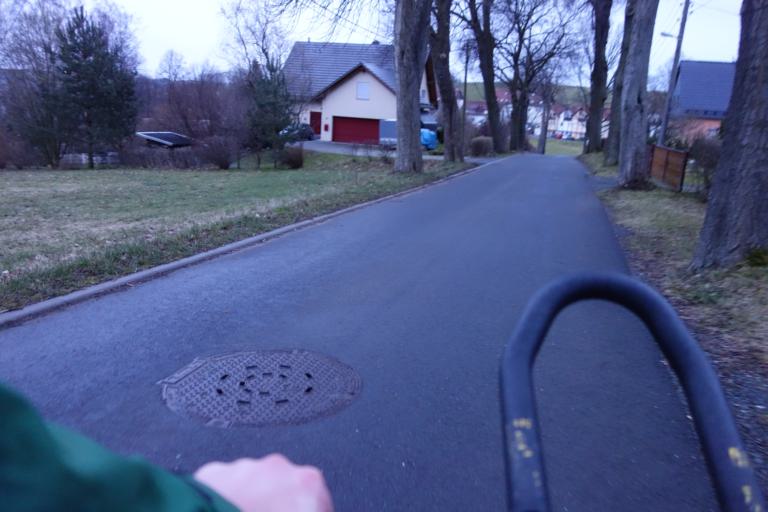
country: DE
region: Saxony
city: Freiberg
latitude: 50.8901
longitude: 13.3733
